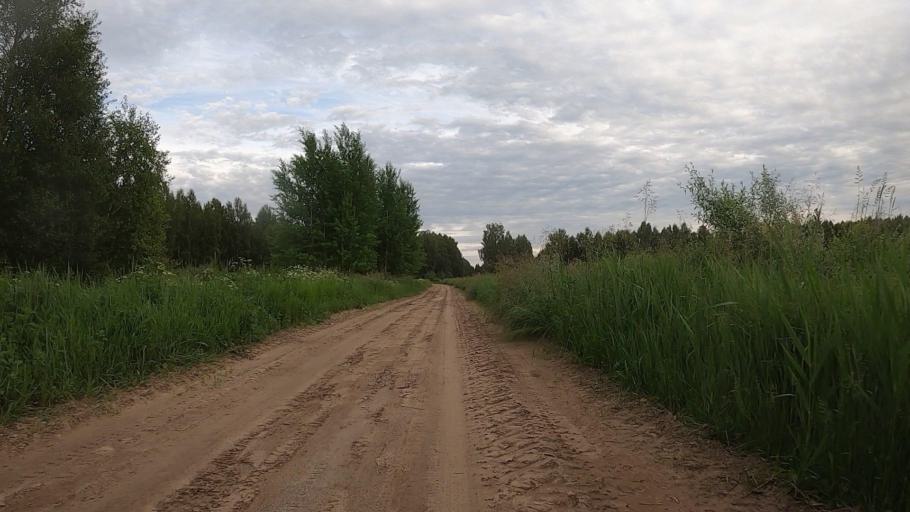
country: LV
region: Olaine
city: Olaine
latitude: 56.8246
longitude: 23.9684
